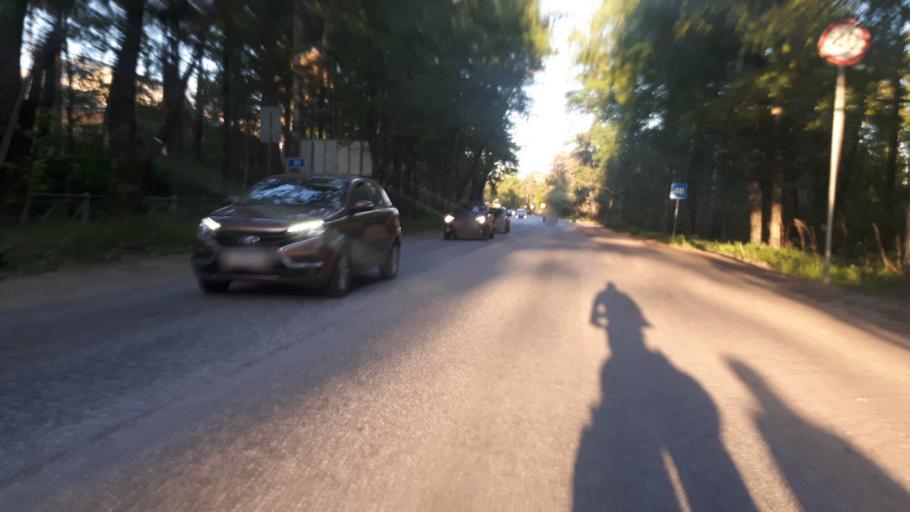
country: RU
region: St.-Petersburg
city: Bol'shaya Izhora
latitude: 59.9453
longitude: 29.5684
